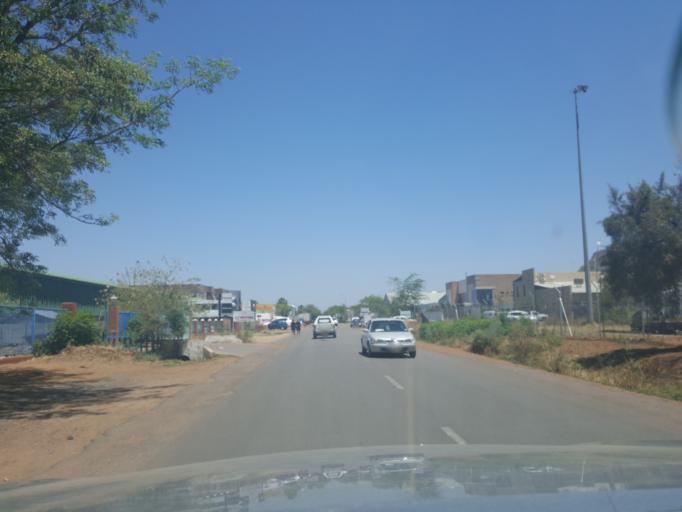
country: BW
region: South East
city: Gaborone
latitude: -24.6830
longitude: 25.8906
